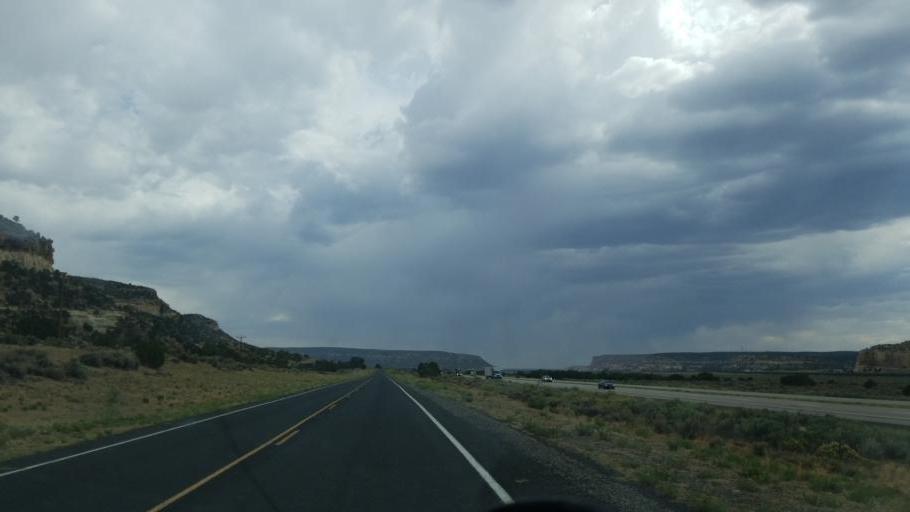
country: US
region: Arizona
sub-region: Apache County
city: Houck
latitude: 35.4075
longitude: -108.9992
